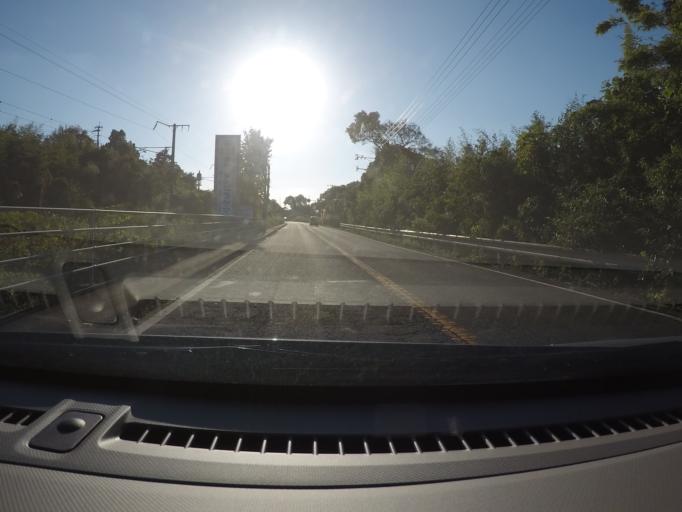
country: JP
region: Kagoshima
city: Izumi
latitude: 32.1488
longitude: 130.3611
